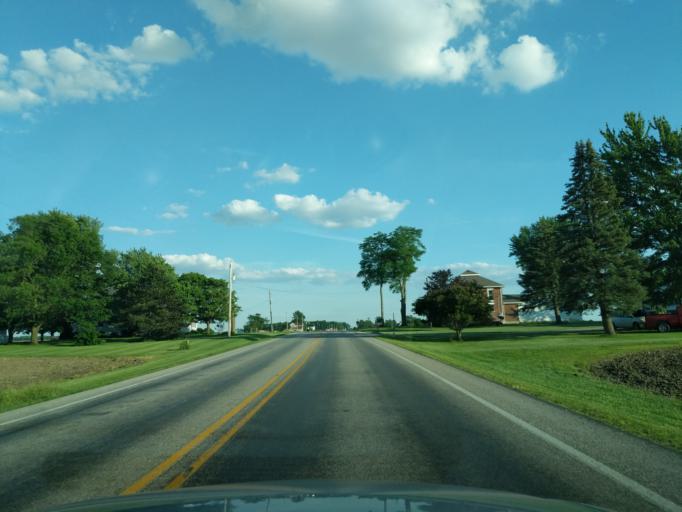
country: US
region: Indiana
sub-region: Huntington County
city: Huntington
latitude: 40.8137
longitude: -85.4651
